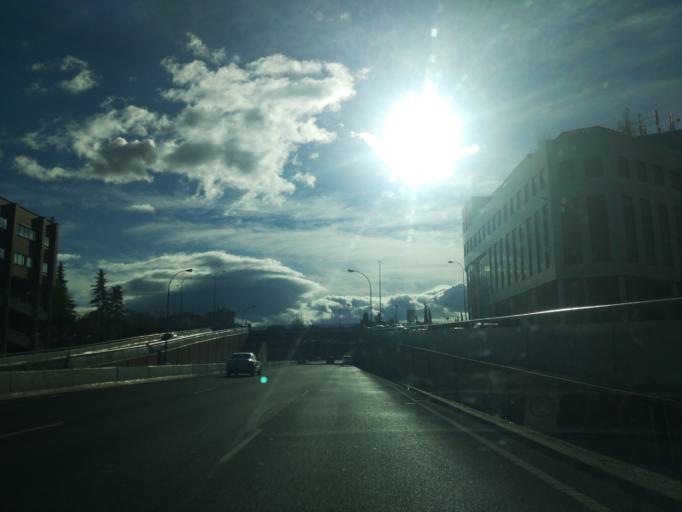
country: ES
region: Madrid
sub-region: Provincia de Madrid
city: Usera
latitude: 40.3776
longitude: -3.6937
